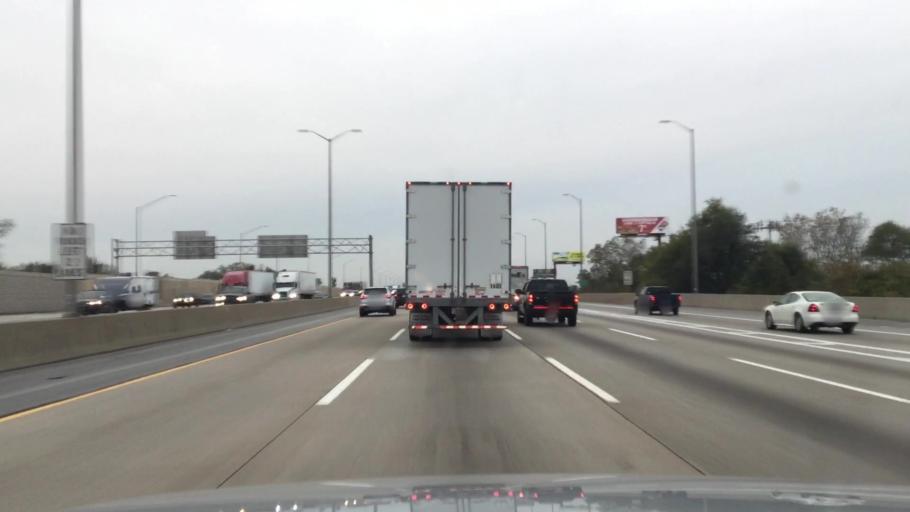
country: US
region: Illinois
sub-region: Cook County
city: East Hazel Crest
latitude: 41.5783
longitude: -87.6443
